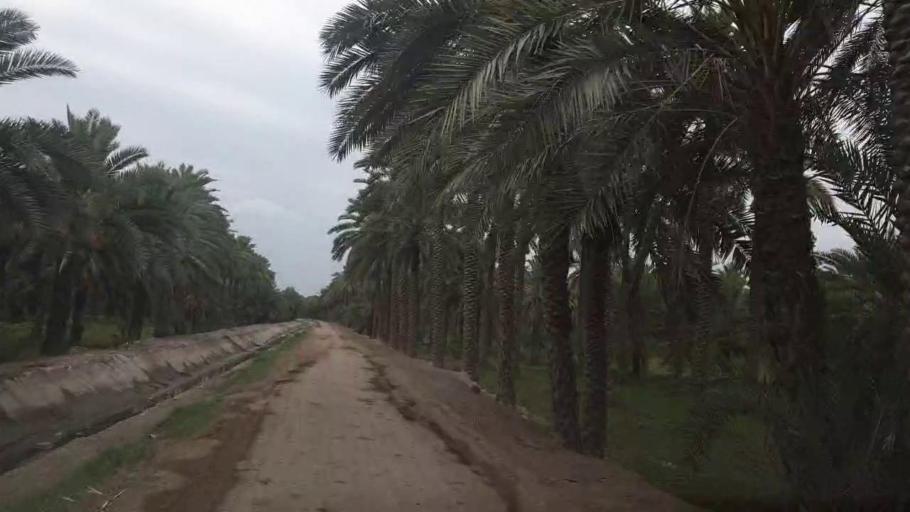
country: PK
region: Sindh
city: Khairpur
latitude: 27.5987
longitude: 68.8011
